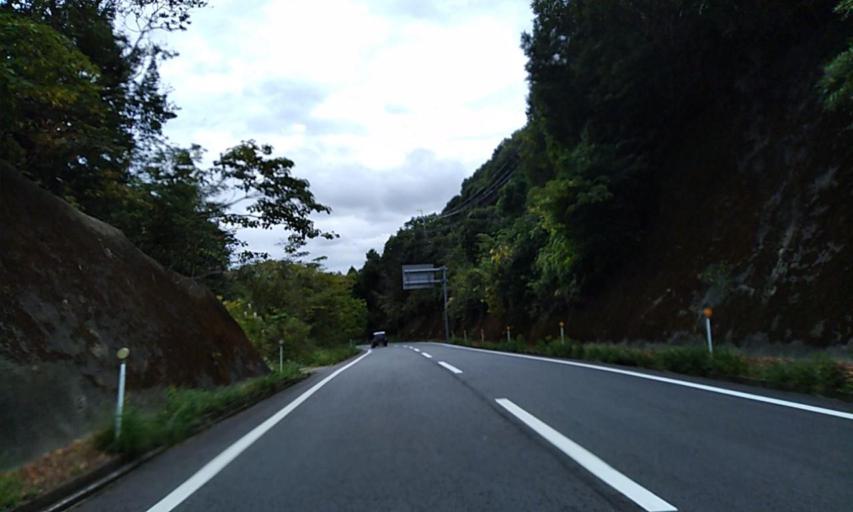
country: JP
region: Wakayama
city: Shingu
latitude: 33.4711
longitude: 135.8183
